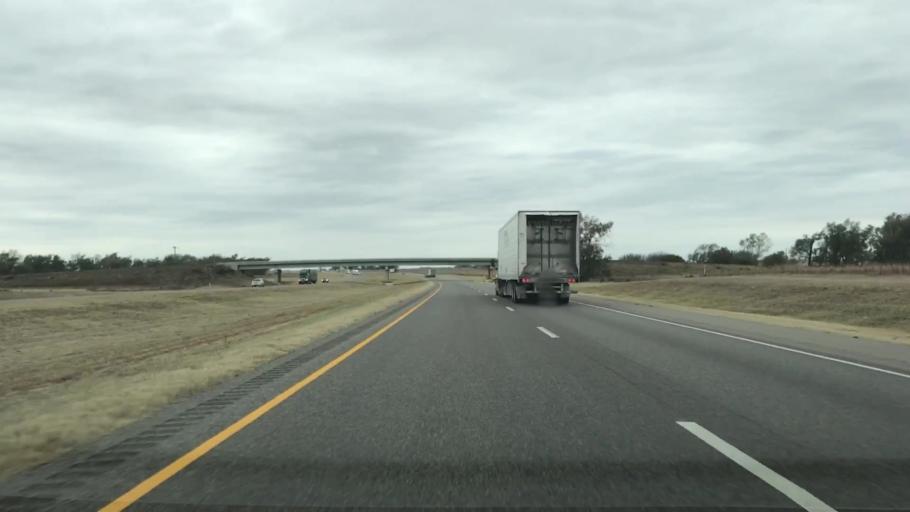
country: US
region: Oklahoma
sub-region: Beckham County
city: Erick
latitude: 35.2313
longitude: -99.9443
